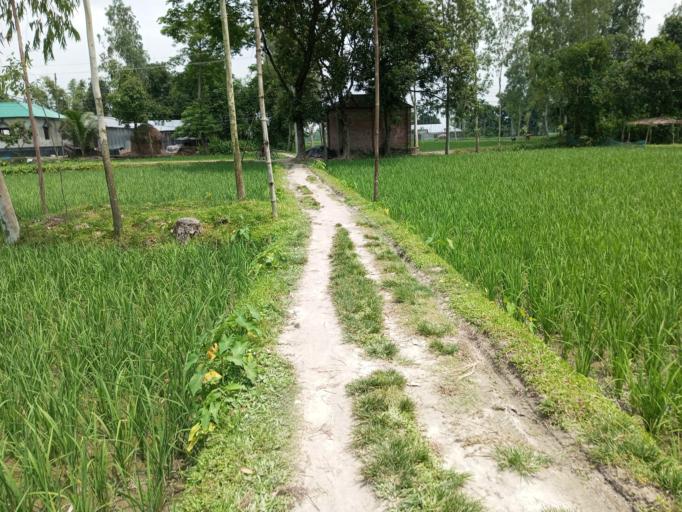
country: BD
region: Rangpur Division
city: Rangpur
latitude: 25.9059
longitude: 89.2688
